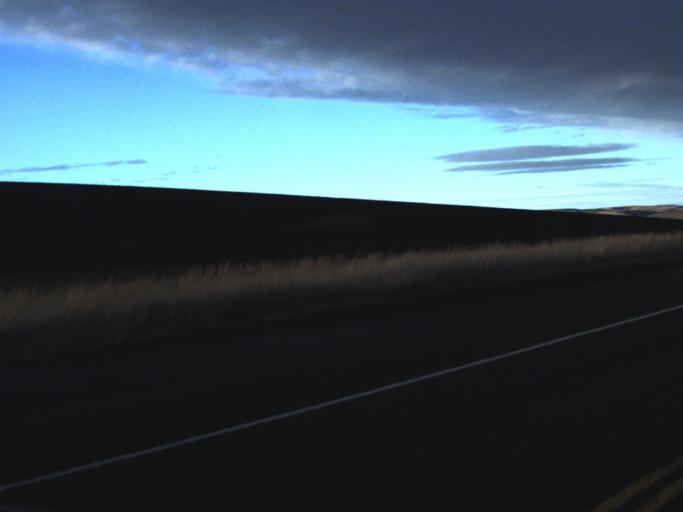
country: US
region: Washington
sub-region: Garfield County
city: Pomeroy
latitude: 46.5777
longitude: -117.7761
